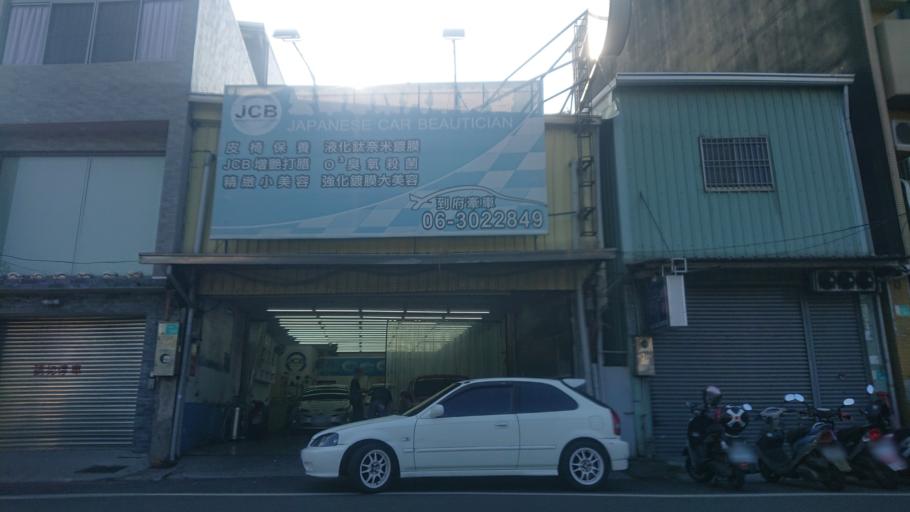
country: TW
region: Taiwan
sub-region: Tainan
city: Tainan
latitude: 23.0181
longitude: 120.2399
